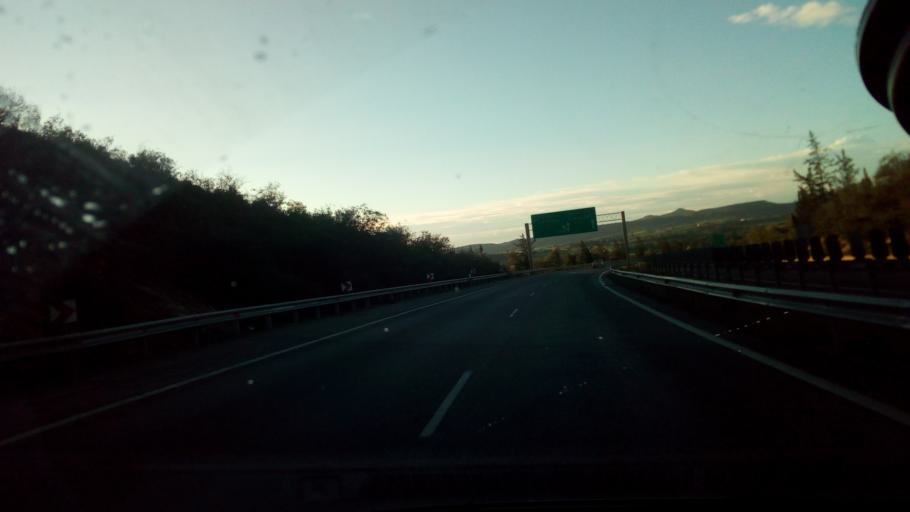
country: CY
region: Larnaka
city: Kofinou
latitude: 34.8457
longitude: 33.4050
